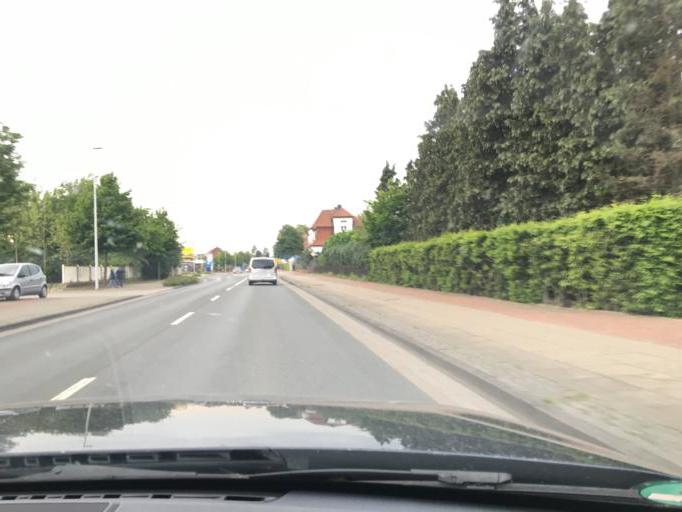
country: DE
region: North Rhine-Westphalia
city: Emsdetten
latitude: 52.1651
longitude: 7.5442
